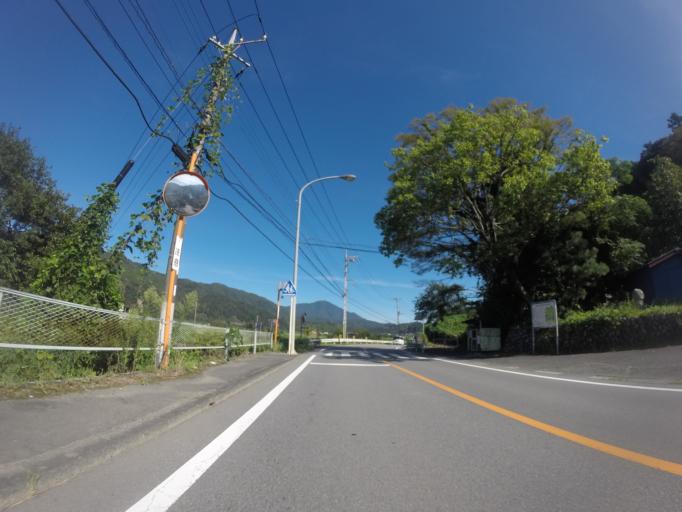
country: JP
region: Shizuoka
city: Fujinomiya
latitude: 35.3238
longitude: 138.4516
